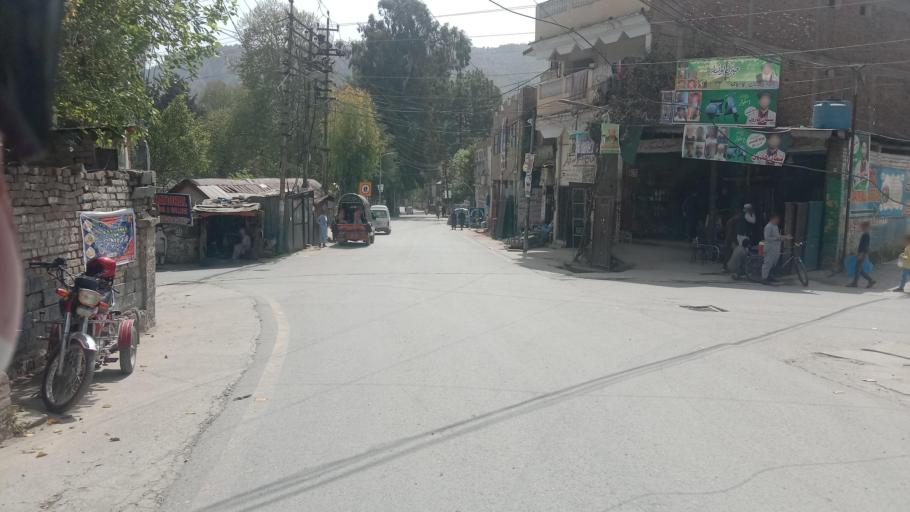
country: PK
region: Khyber Pakhtunkhwa
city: Abbottabad
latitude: 34.1474
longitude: 73.2059
